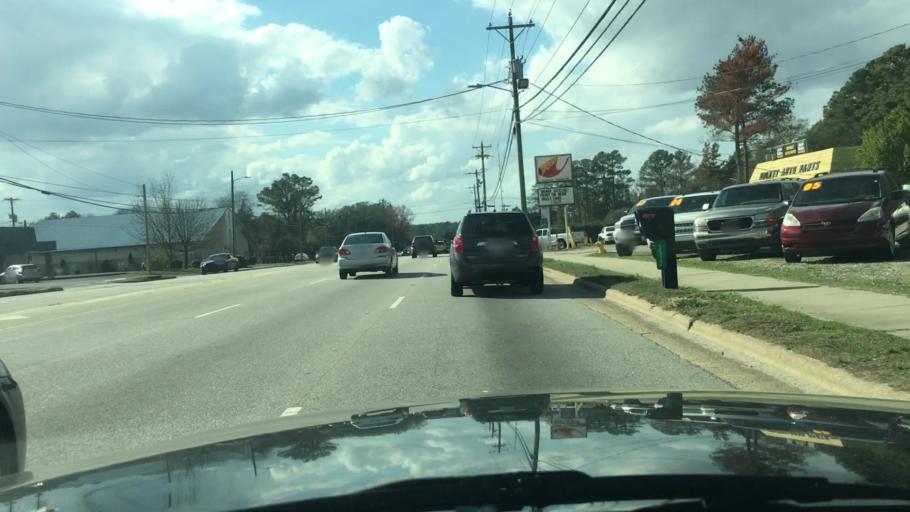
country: US
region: North Carolina
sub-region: Cumberland County
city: Hope Mills
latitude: 35.0427
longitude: -78.9685
